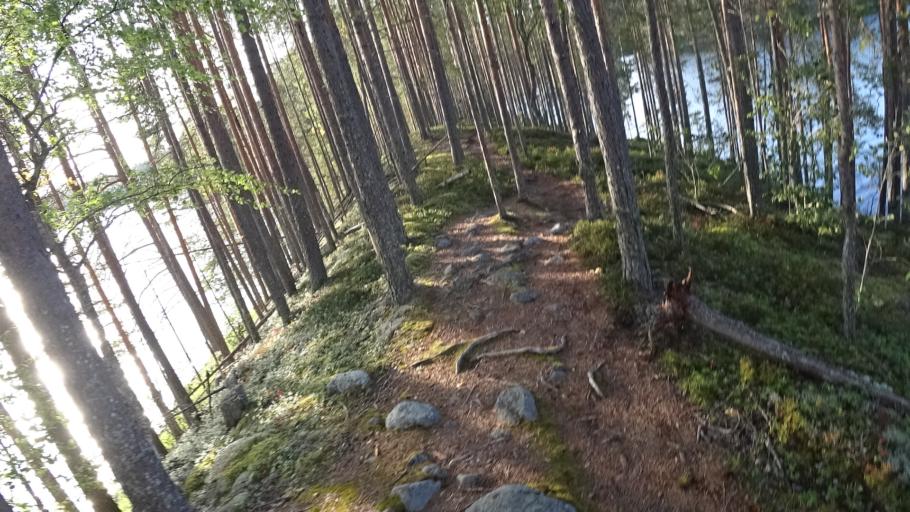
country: FI
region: North Karelia
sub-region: Joensuu
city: Ilomantsi
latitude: 62.5772
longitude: 31.1718
